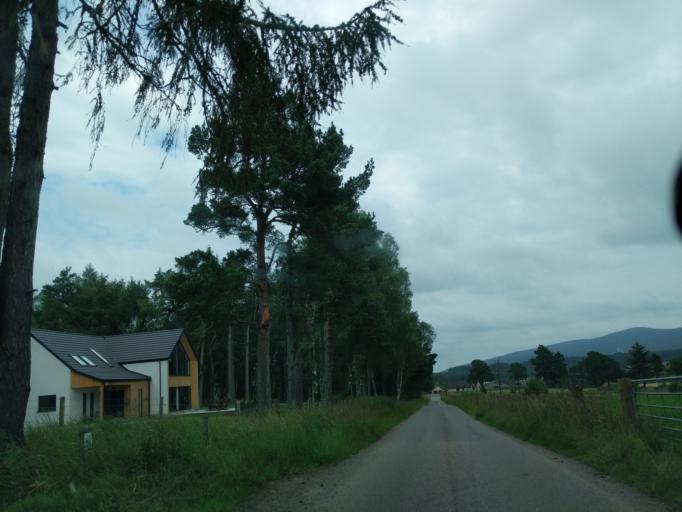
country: GB
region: Scotland
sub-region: Moray
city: Rothes
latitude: 57.4836
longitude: -3.2316
